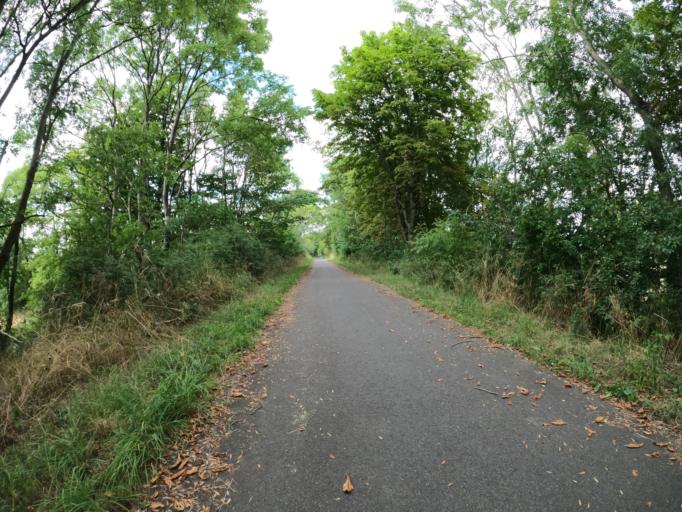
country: DE
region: Mecklenburg-Vorpommern
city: Woldegk
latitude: 53.3809
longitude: 13.5888
